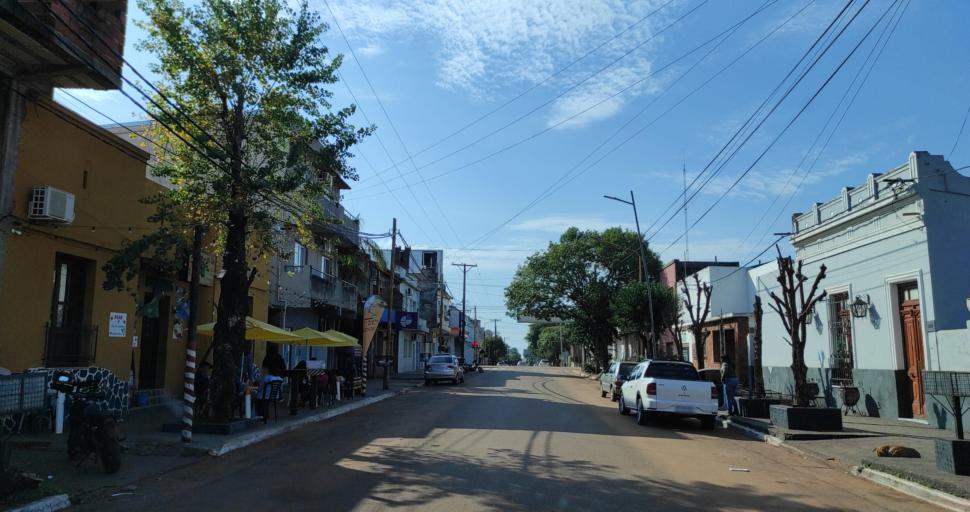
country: AR
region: Corrientes
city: Santo Tome
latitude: -28.5503
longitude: -56.0376
